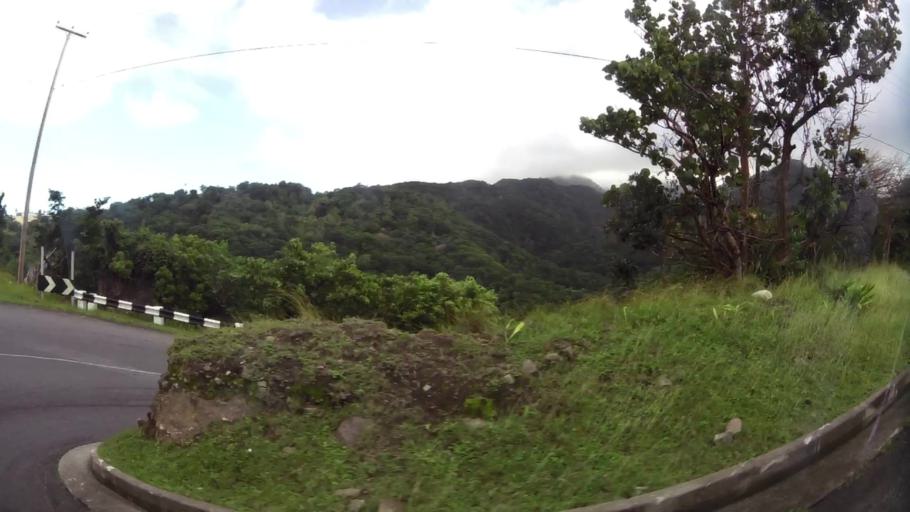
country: MS
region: Saint Peter
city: Saint Peters
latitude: 16.7772
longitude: -62.2101
